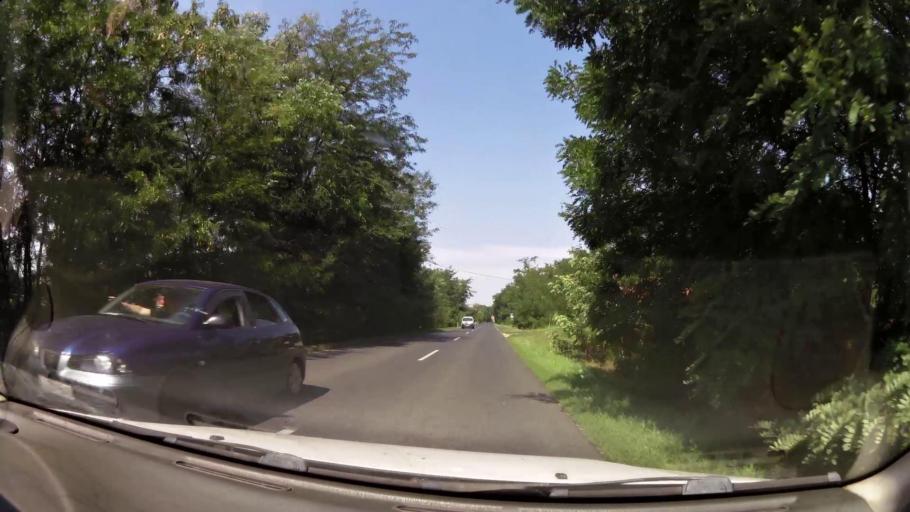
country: HU
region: Pest
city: Tapiosag
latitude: 47.4121
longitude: 19.6113
